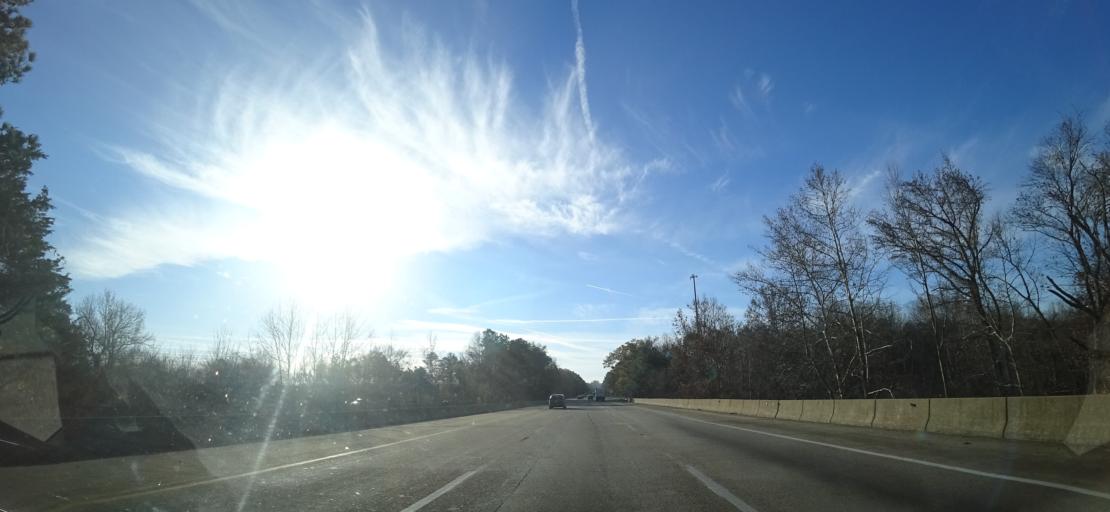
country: US
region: Virginia
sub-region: Hanover County
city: Ashland
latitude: 37.8909
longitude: -77.4585
